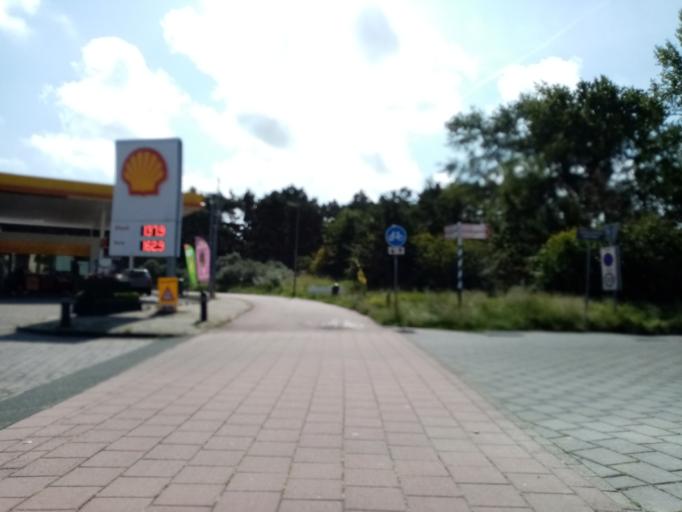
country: NL
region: North Holland
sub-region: Gemeente Zandvoort
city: Zandvoort
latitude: 52.3671
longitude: 4.5423
